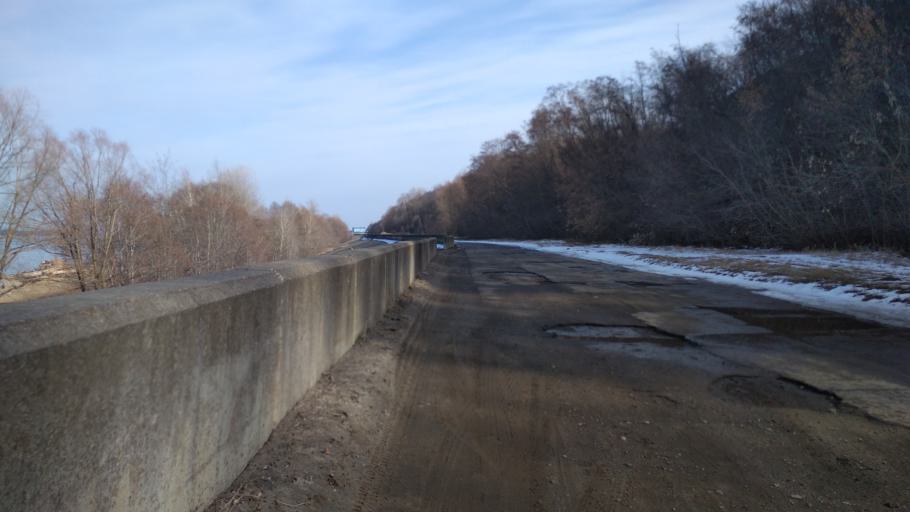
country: RU
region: Chuvashia
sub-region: Cheboksarskiy Rayon
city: Cheboksary
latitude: 56.1465
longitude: 47.3070
